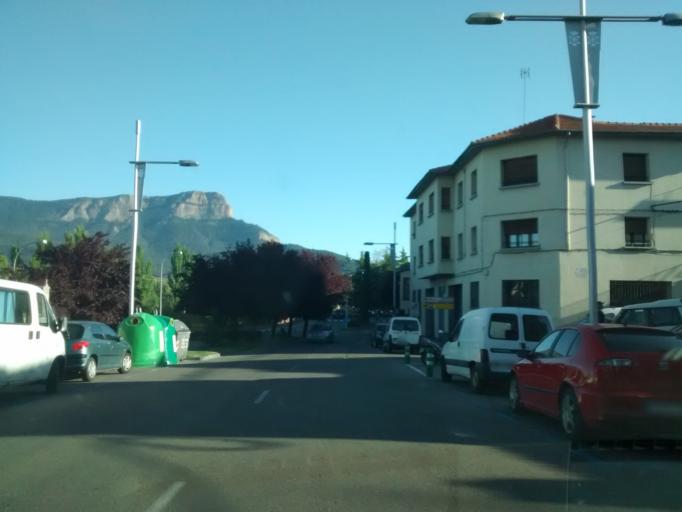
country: ES
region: Aragon
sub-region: Provincia de Huesca
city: Jaca
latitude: 42.5698
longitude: -0.5463
